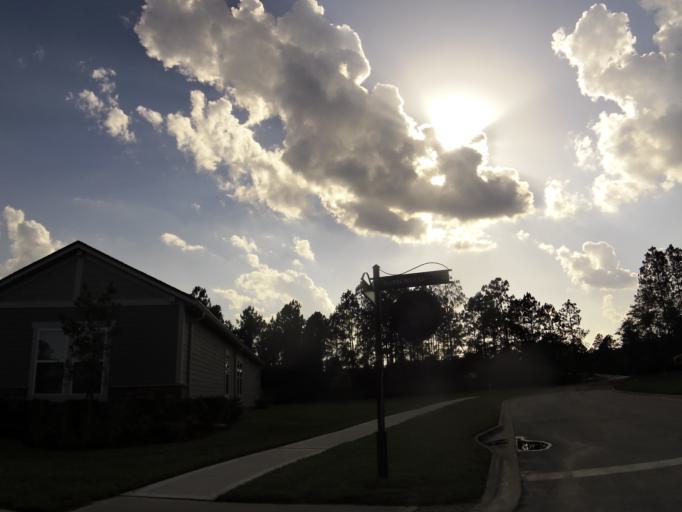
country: US
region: Florida
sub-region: Clay County
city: Green Cove Springs
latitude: 30.0287
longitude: -81.6352
